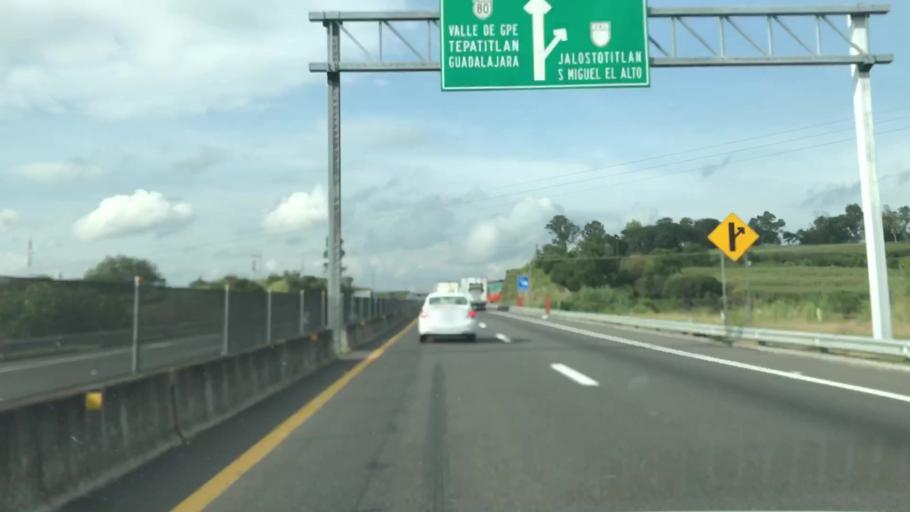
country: MX
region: Jalisco
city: Jalostotitlan
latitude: 21.1222
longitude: -102.4534
